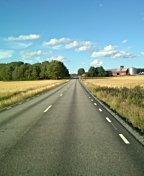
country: SE
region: Uppsala
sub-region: Habo Kommun
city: Balsta
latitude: 59.6416
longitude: 17.5289
